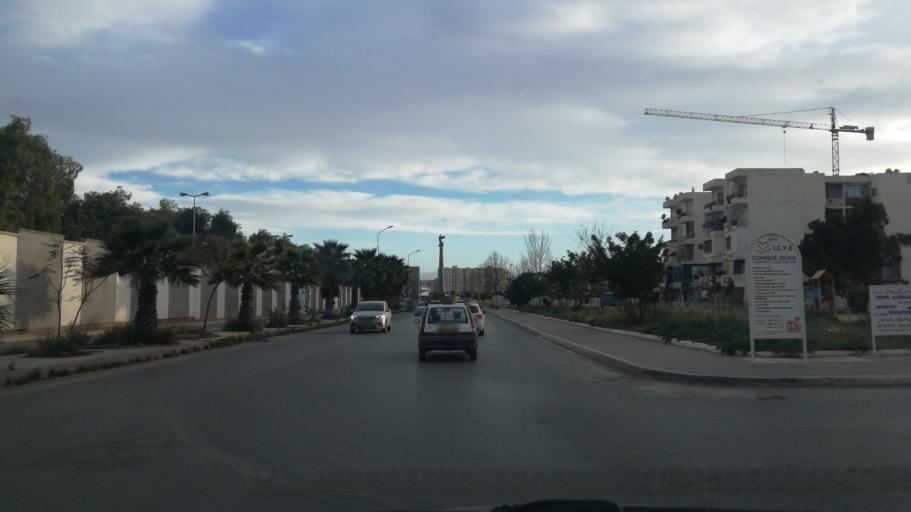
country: DZ
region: Oran
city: Bir el Djir
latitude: 35.6985
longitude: -0.5852
